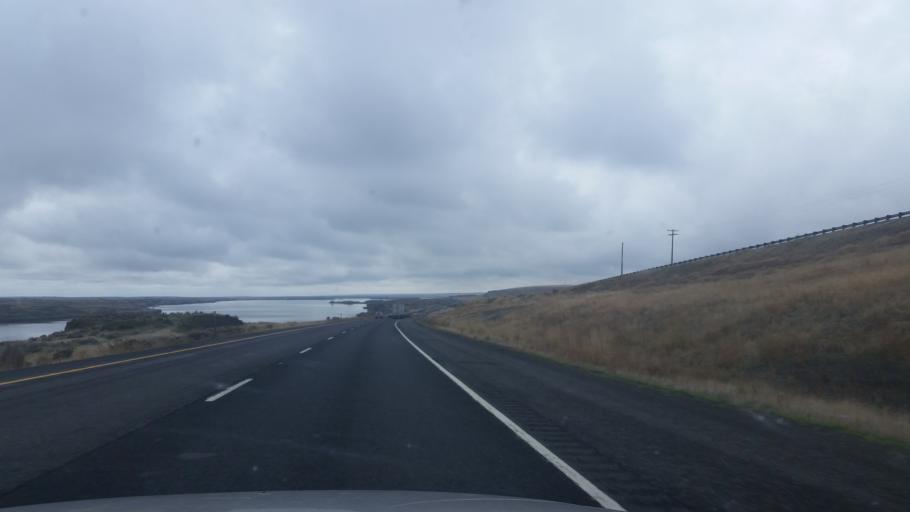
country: US
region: Washington
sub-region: Adams County
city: Ritzville
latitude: 47.2884
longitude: -118.0383
